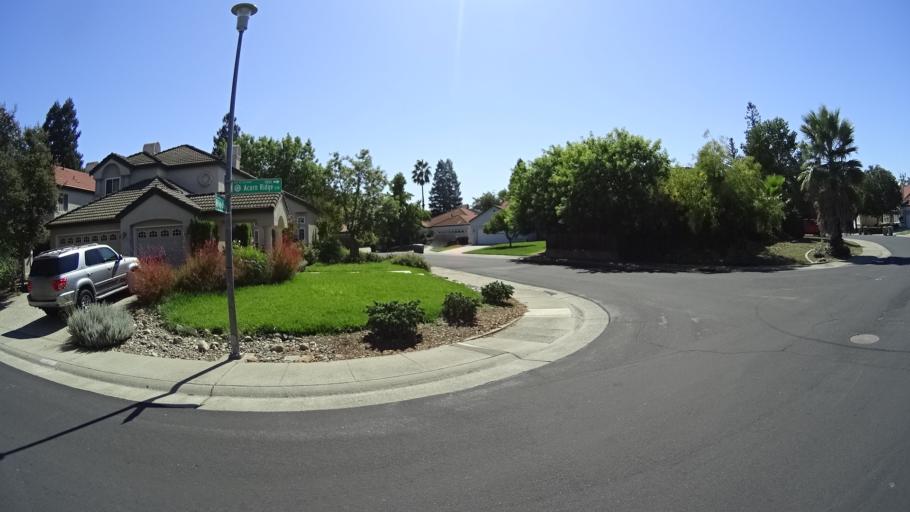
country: US
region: California
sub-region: Sacramento County
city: Laguna
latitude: 38.4294
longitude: -121.4333
